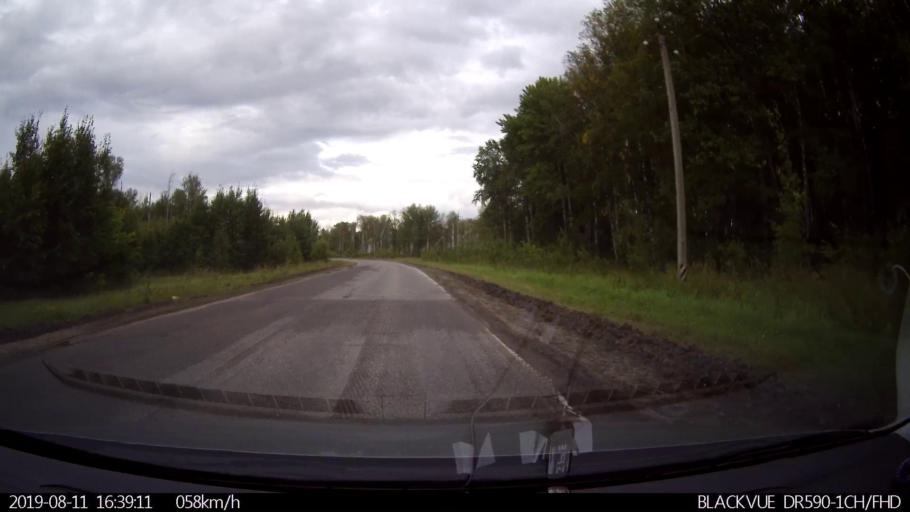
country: RU
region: Ulyanovsk
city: Mayna
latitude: 54.1385
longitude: 47.6344
